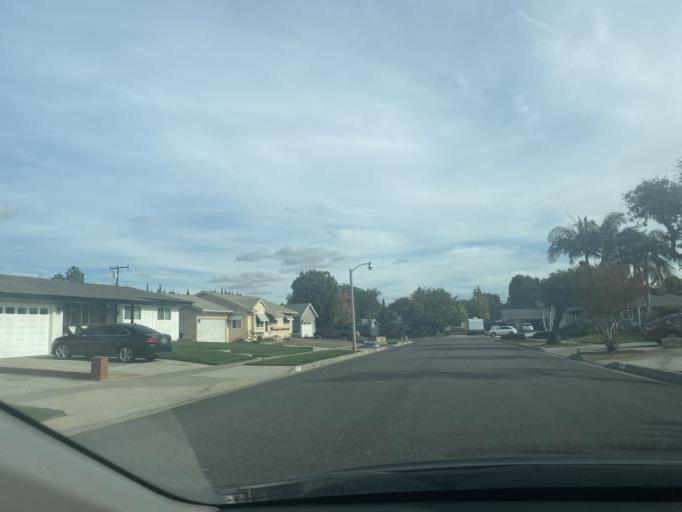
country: US
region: California
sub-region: Orange County
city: Brea
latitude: 33.9057
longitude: -117.8996
